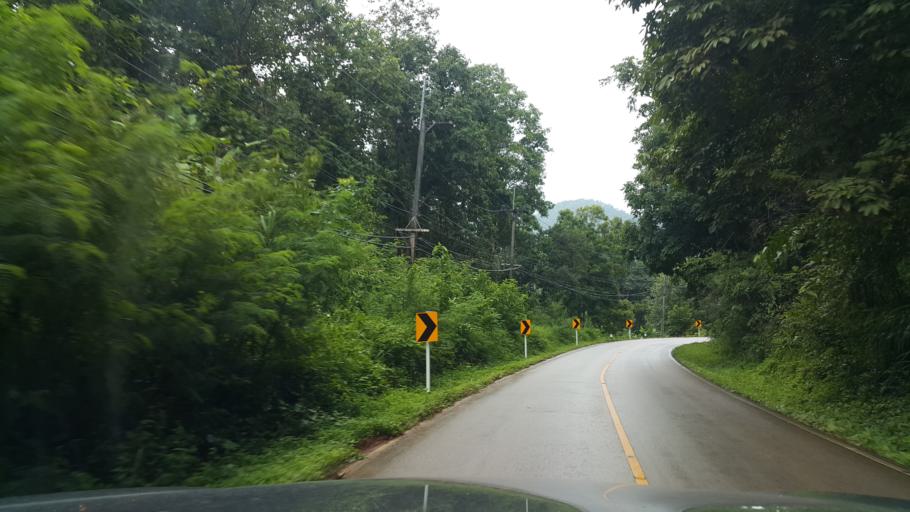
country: TH
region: Chiang Mai
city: Samoeng
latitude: 18.8630
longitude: 98.7126
